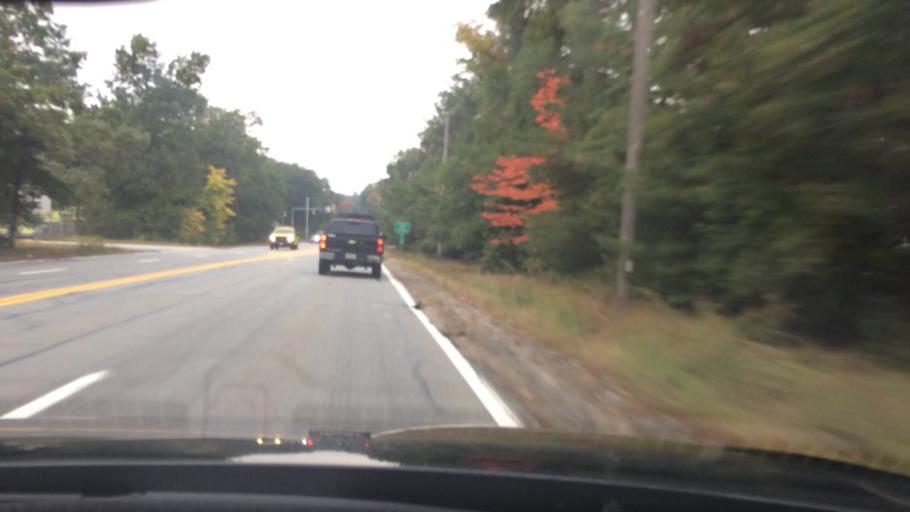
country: US
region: Massachusetts
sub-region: Middlesex County
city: Chelmsford
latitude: 42.6258
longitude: -71.3679
